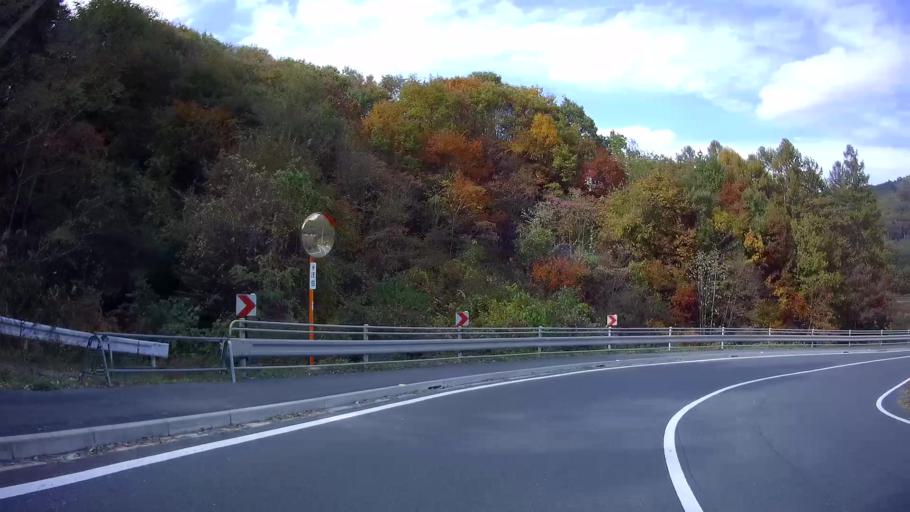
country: JP
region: Gunma
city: Nakanojomachi
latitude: 36.5413
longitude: 138.6585
